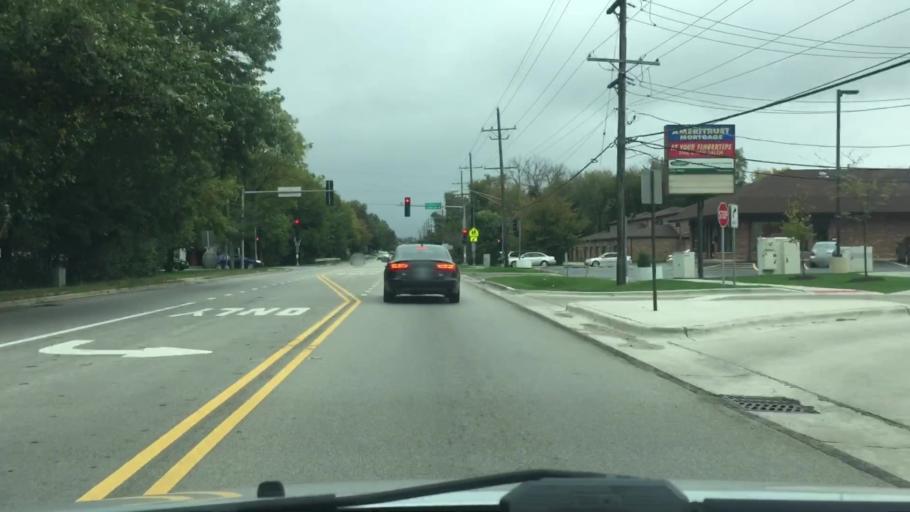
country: US
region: Illinois
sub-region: McHenry County
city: McHenry
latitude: 42.3369
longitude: -88.2746
